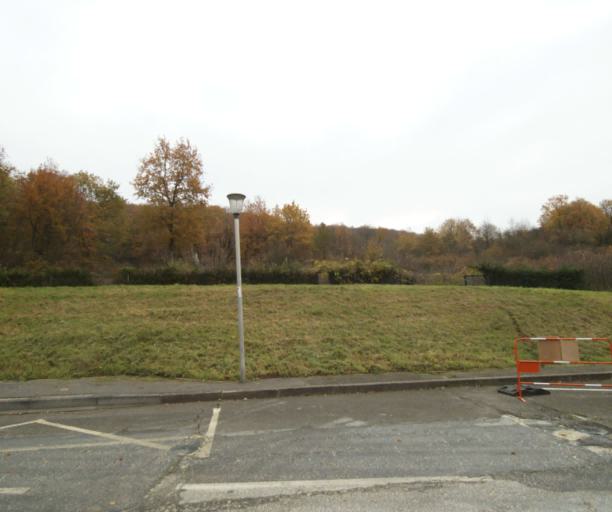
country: FR
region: Ile-de-France
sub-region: Departement des Yvelines
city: Triel-sur-Seine
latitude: 48.9817
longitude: 2.0177
